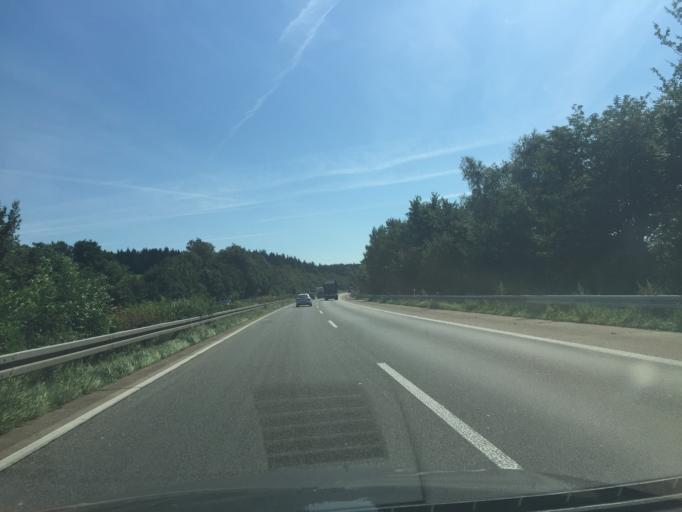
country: DE
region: North Rhine-Westphalia
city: Meinerzhagen
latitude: 51.1413
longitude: 7.6756
